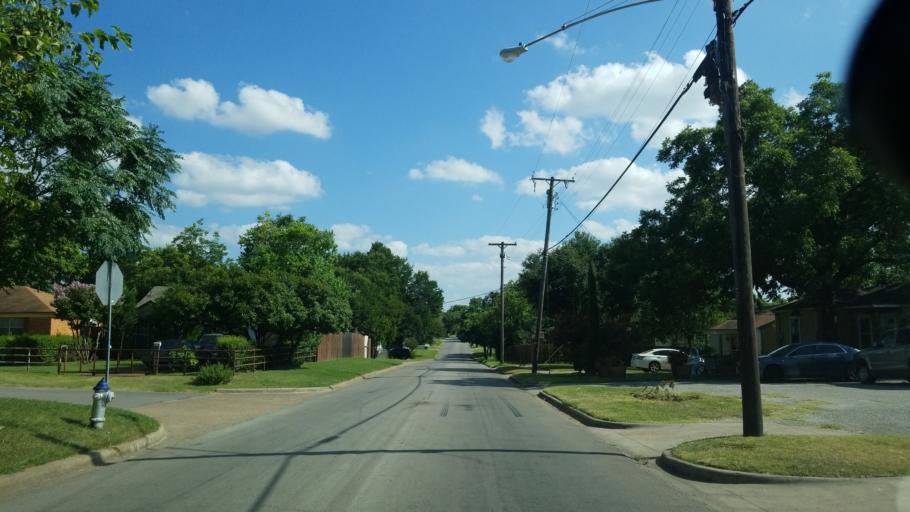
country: US
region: Texas
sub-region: Dallas County
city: Balch Springs
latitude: 32.7726
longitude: -96.7050
